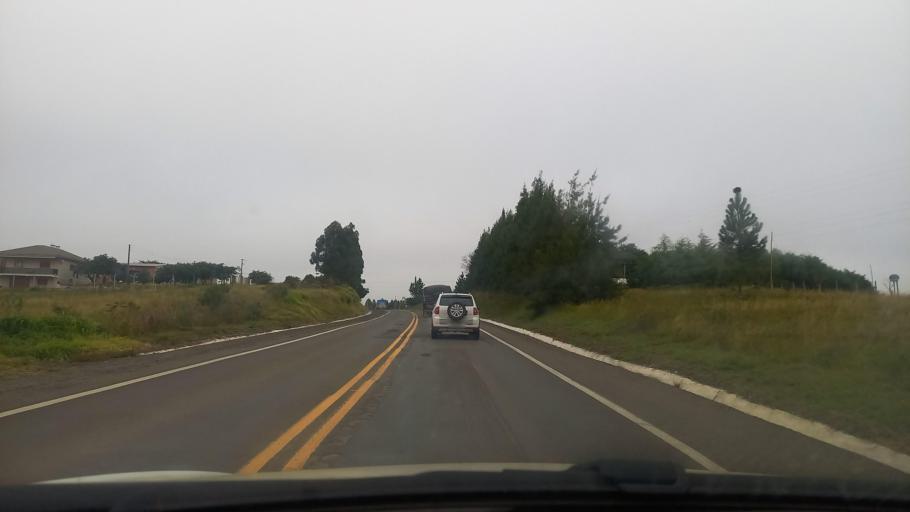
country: BR
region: Rio Grande do Sul
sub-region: Rosario Do Sul
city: Rosario do Sul
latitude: -30.2687
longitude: -54.9746
